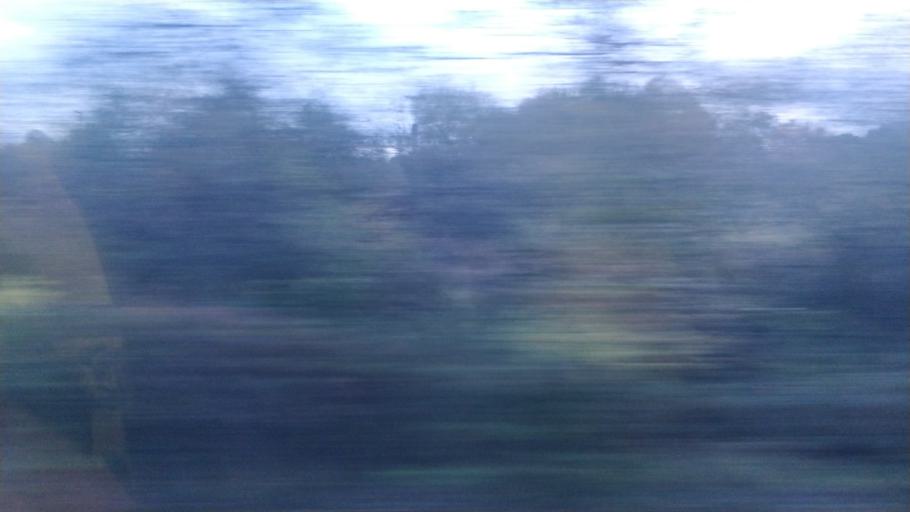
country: GB
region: England
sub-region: Borough of Wigan
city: Shevington
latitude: 53.5577
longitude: -2.6822
